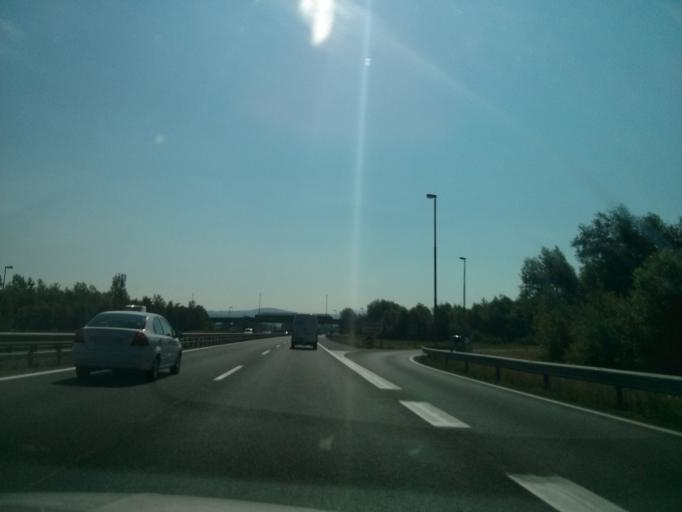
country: SI
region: Ljubljana
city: Ljubljana
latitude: 46.0260
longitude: 14.4958
